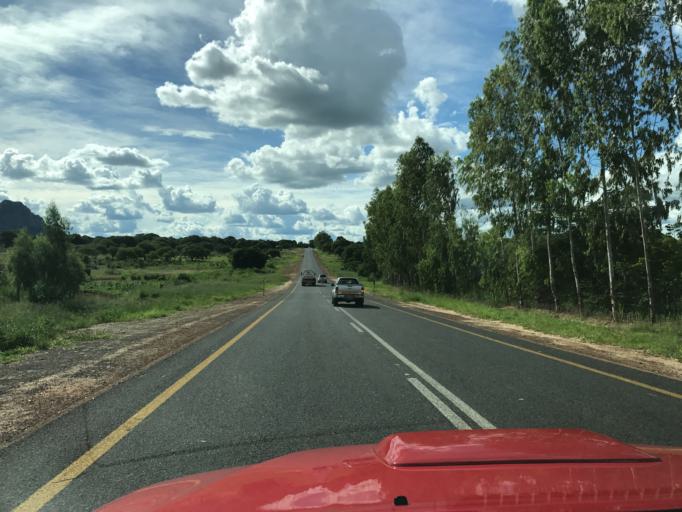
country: MZ
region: Nampula
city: Nampula
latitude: -15.0400
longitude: 39.1347
